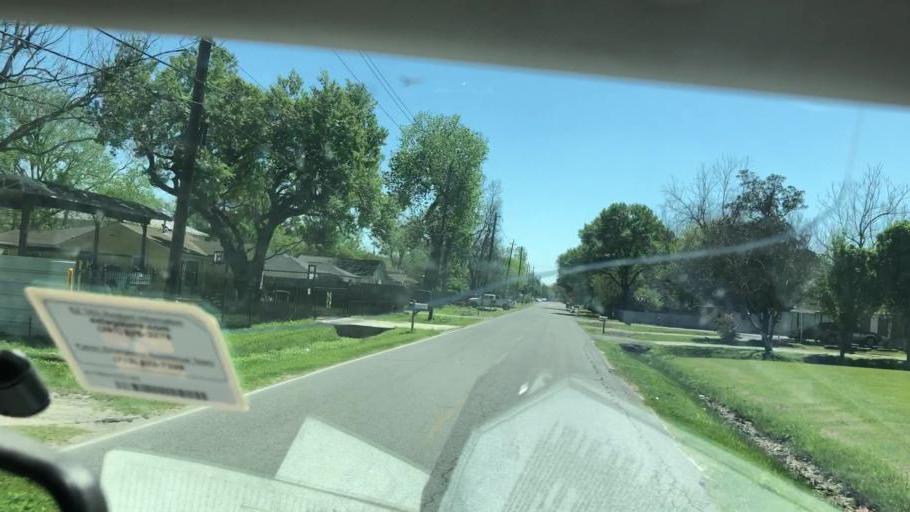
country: US
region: Texas
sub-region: Harris County
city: Aldine
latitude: 29.9051
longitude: -95.3910
